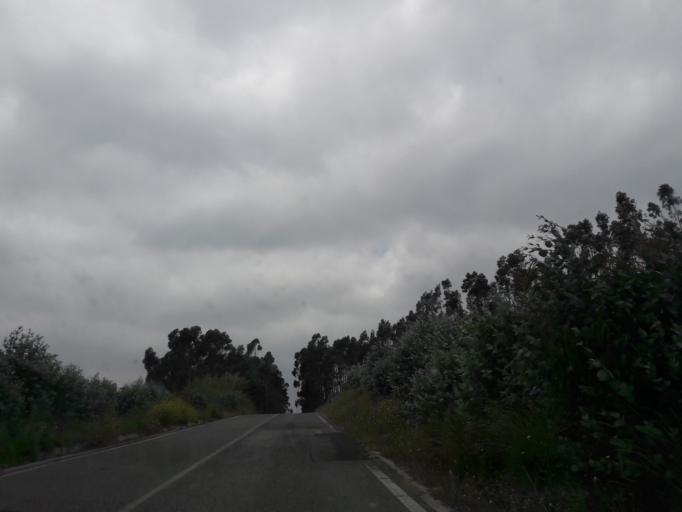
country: PT
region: Leiria
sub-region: Peniche
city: Atouguia da Baleia
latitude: 39.3452
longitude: -9.2816
